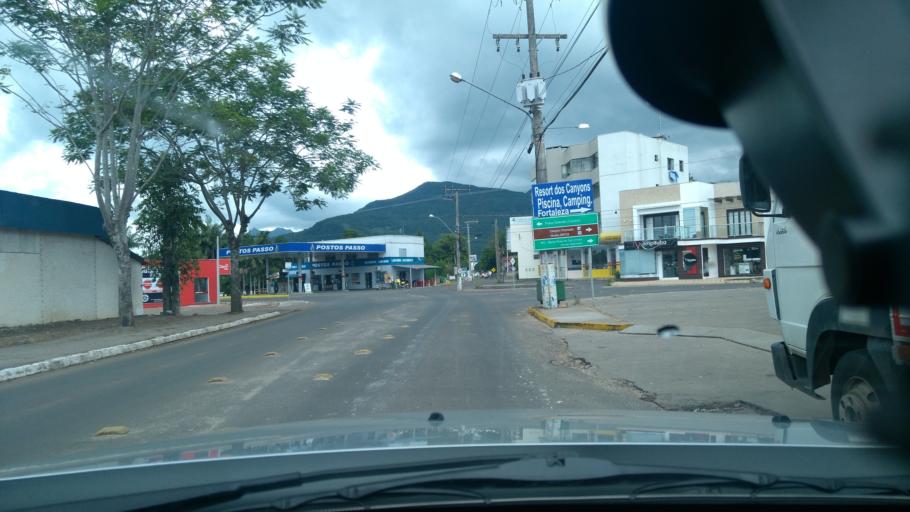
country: BR
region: Rio Grande do Sul
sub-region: Torres
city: Torres
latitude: -29.1952
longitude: -49.9470
